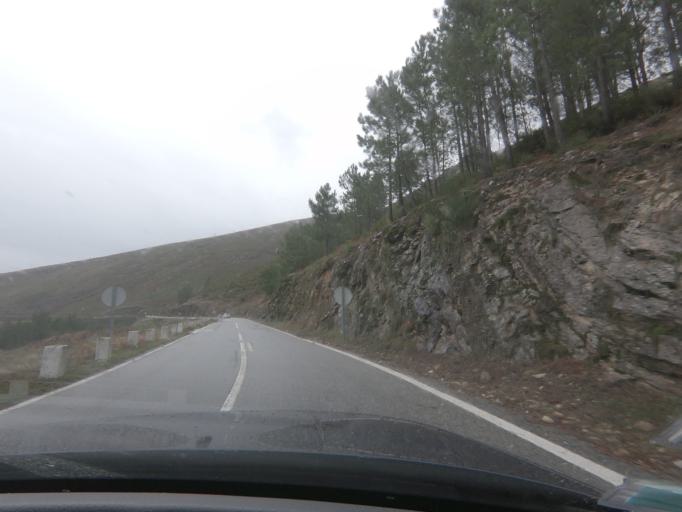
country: PT
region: Vila Real
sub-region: Mondim de Basto
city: Mondim de Basto
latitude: 41.3502
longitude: -7.8764
